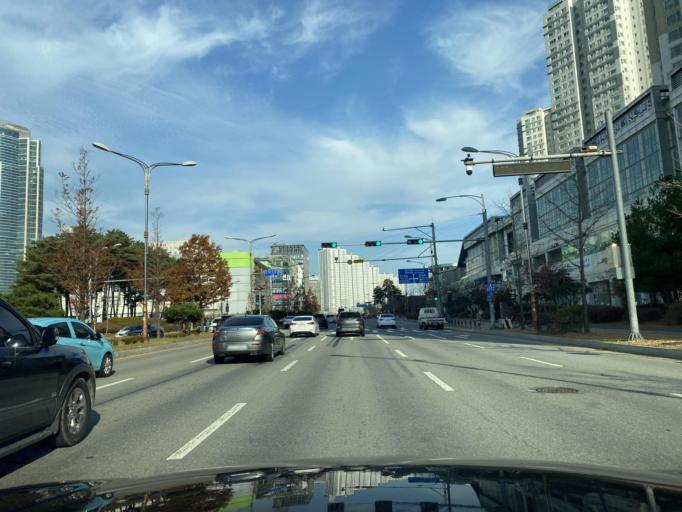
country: KR
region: Chungcheongnam-do
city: Cheonan
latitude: 36.7943
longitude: 127.1072
